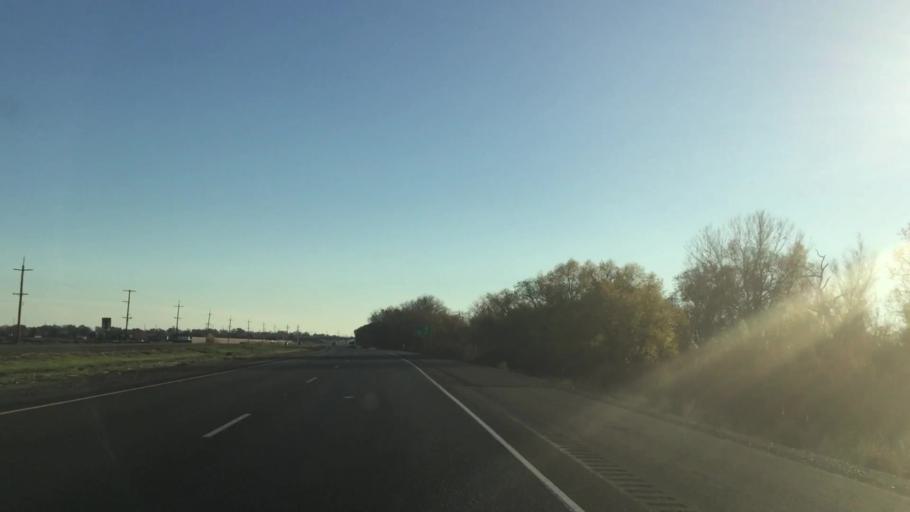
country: US
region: California
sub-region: Yuba County
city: Plumas Lake
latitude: 38.9898
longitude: -121.5436
